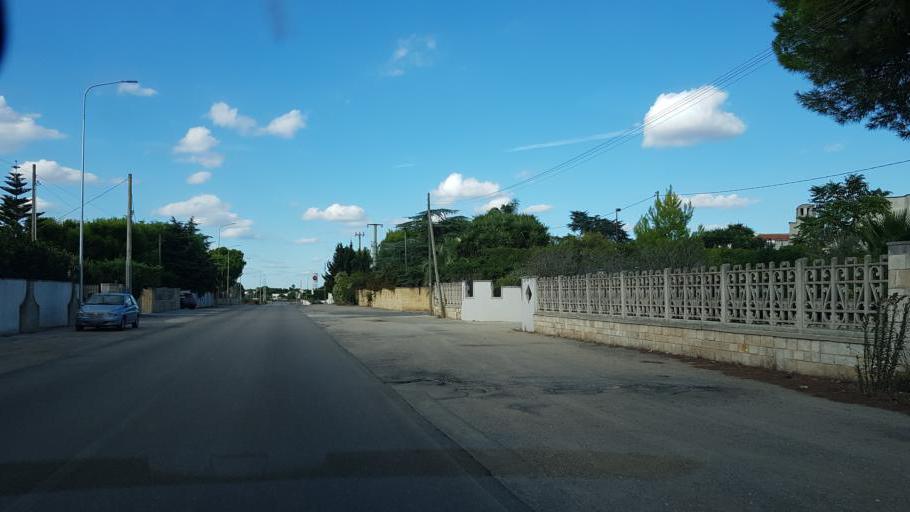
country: IT
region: Apulia
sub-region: Provincia di Lecce
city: Nardo
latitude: 40.1447
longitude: 18.0187
